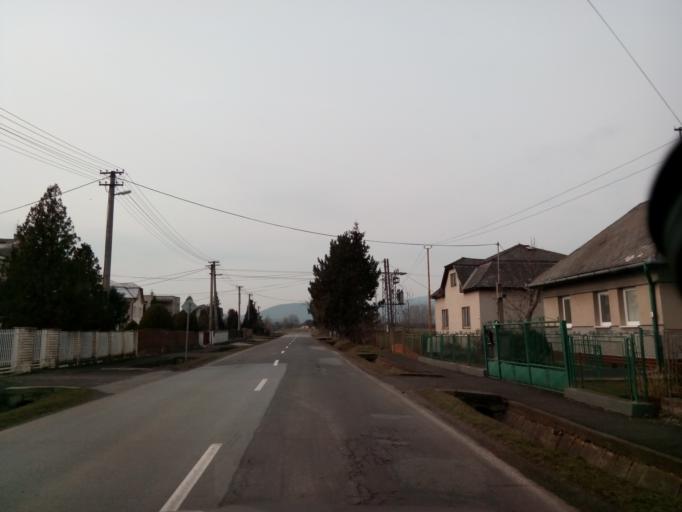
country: SK
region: Kosicky
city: Secovce
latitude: 48.6164
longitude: 21.6000
